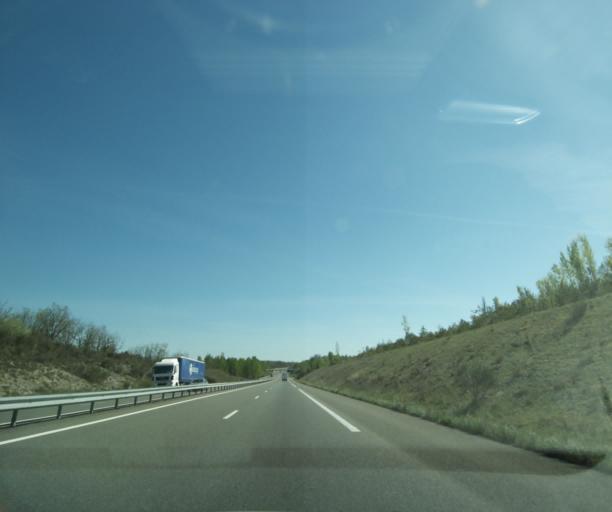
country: FR
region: Midi-Pyrenees
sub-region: Departement du Lot
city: Lalbenque
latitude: 44.3260
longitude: 1.5049
